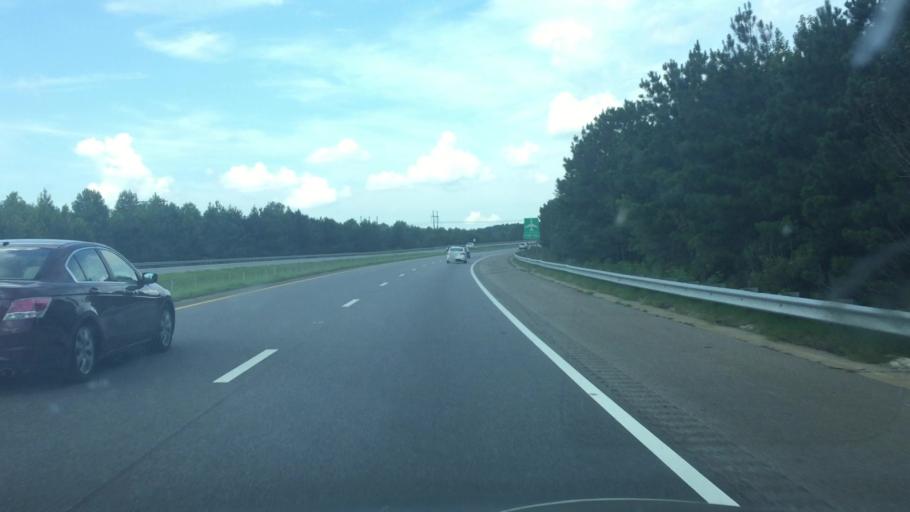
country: US
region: North Carolina
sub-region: Richmond County
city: Hamlet
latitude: 34.8525
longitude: -79.7302
